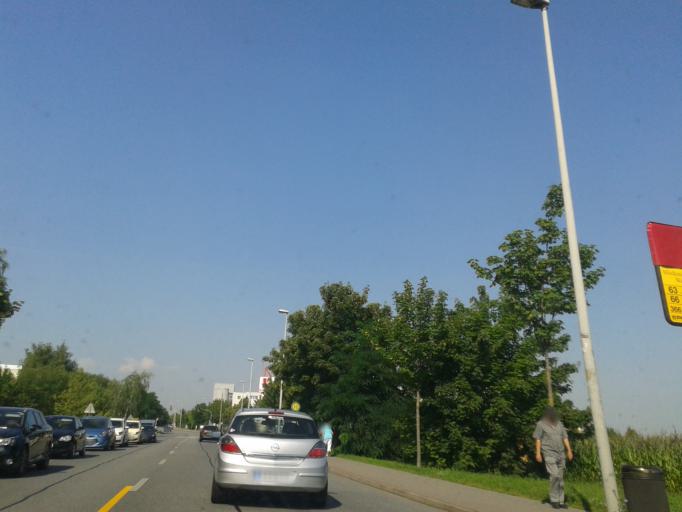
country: DE
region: Saxony
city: Bannewitz
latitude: 51.0194
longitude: 13.7254
